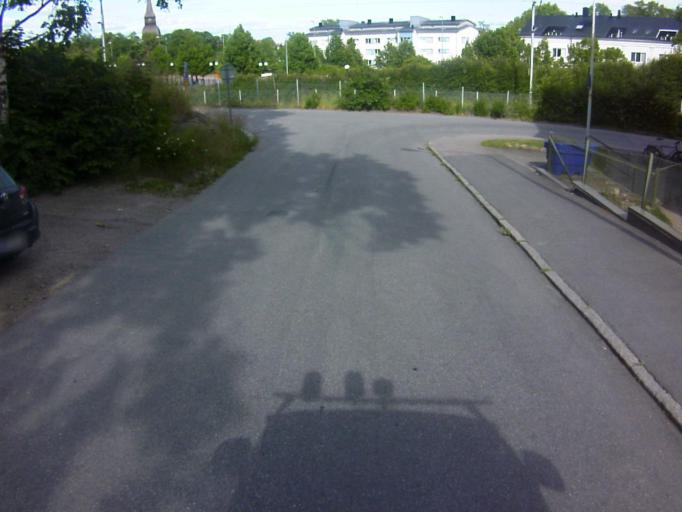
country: SE
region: Soedermanland
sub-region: Eskilstuna Kommun
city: Eskilstuna
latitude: 59.3659
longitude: 16.5107
